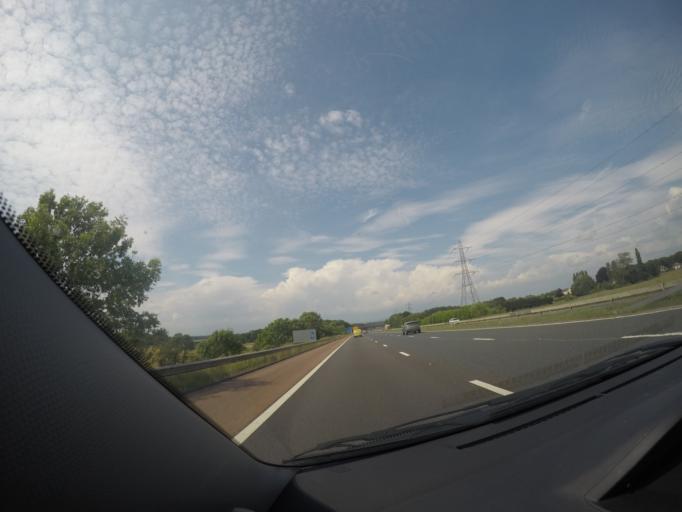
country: GB
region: England
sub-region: Cumbria
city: Scotby
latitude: 54.8885
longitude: -2.8854
